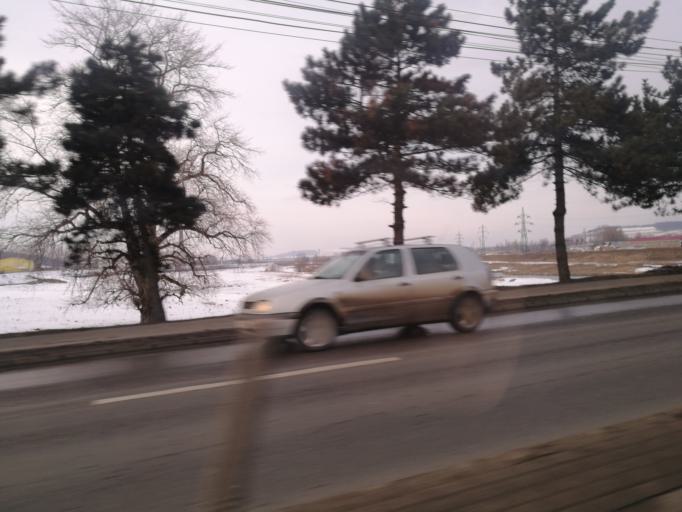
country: RO
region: Suceava
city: Suceava
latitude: 47.6577
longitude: 26.2632
